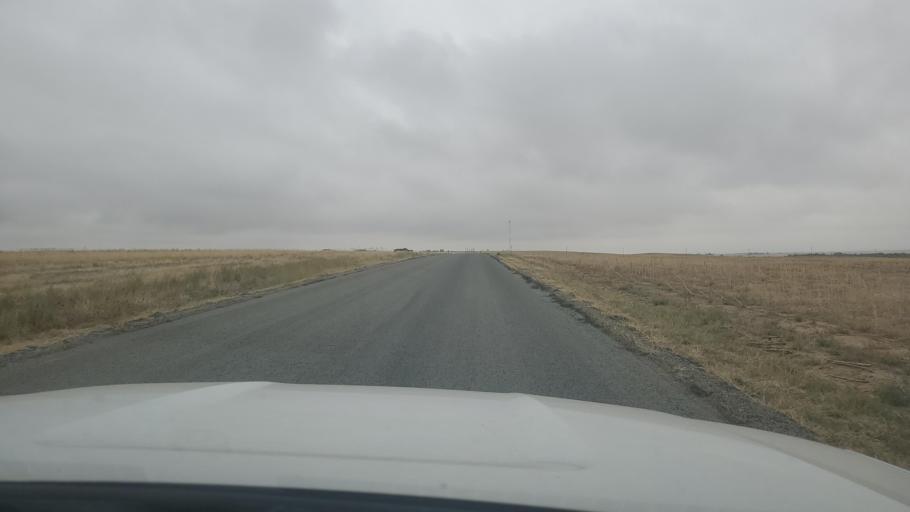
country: US
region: Colorado
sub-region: Weld County
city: Lochbuie
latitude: 39.9348
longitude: -104.6025
